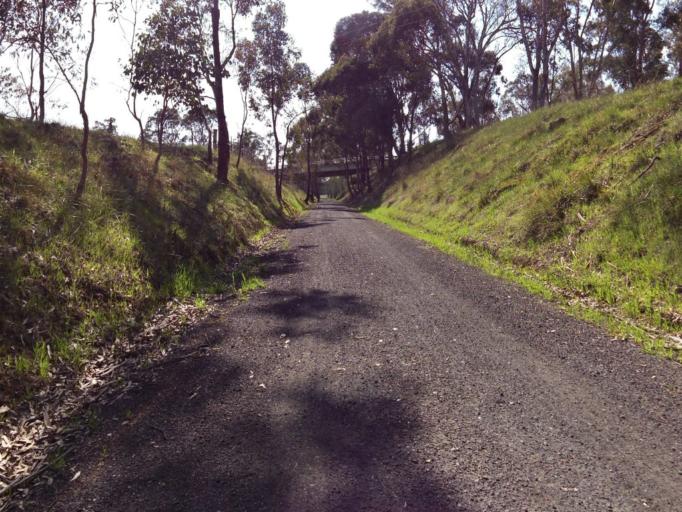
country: AU
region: Victoria
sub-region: Murrindindi
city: Alexandra
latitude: -37.1171
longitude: 145.6053
